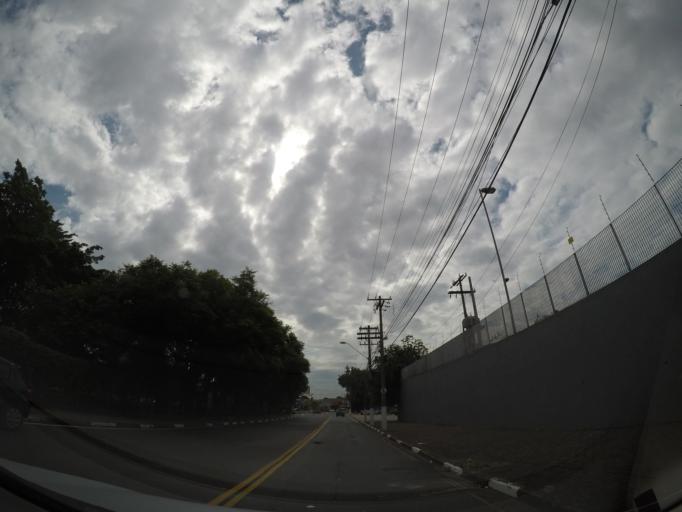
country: BR
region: Sao Paulo
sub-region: Campinas
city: Campinas
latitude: -22.9279
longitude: -47.0400
